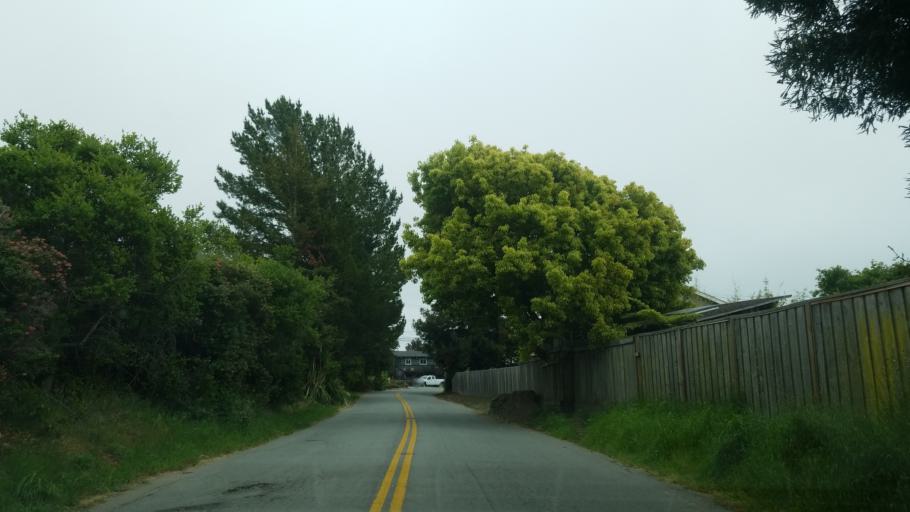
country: US
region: California
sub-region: Santa Cruz County
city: Seacliff
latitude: 36.9773
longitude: -121.9179
